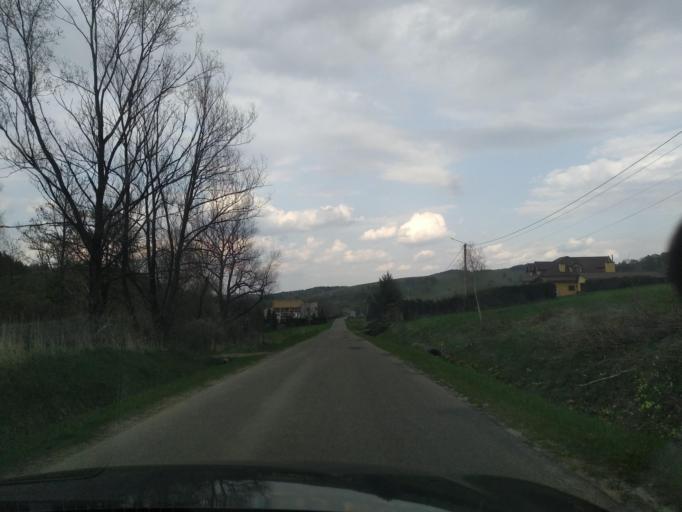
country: PL
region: Subcarpathian Voivodeship
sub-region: Powiat sanocki
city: Czaszyn
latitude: 49.3829
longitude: 22.1950
